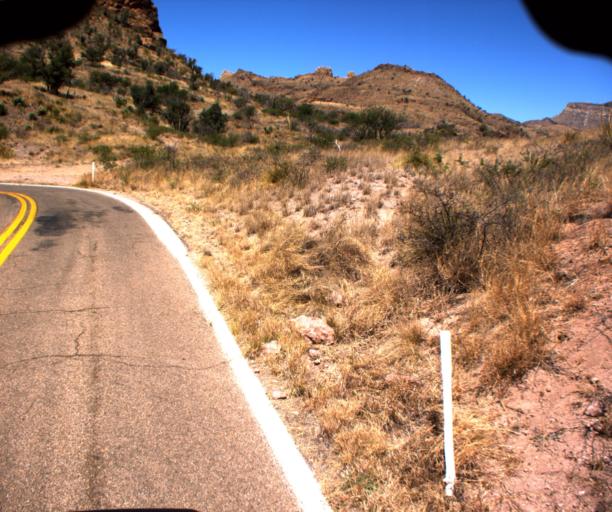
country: US
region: Arizona
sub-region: Santa Cruz County
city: Rio Rico
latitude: 31.3993
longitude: -111.0916
